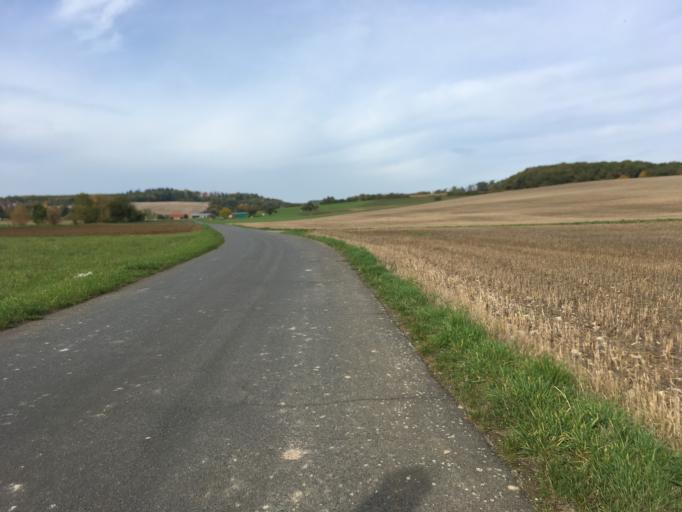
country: DE
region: Baden-Wuerttemberg
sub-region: Karlsruhe Region
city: Rosenberg
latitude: 49.4812
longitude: 9.4660
